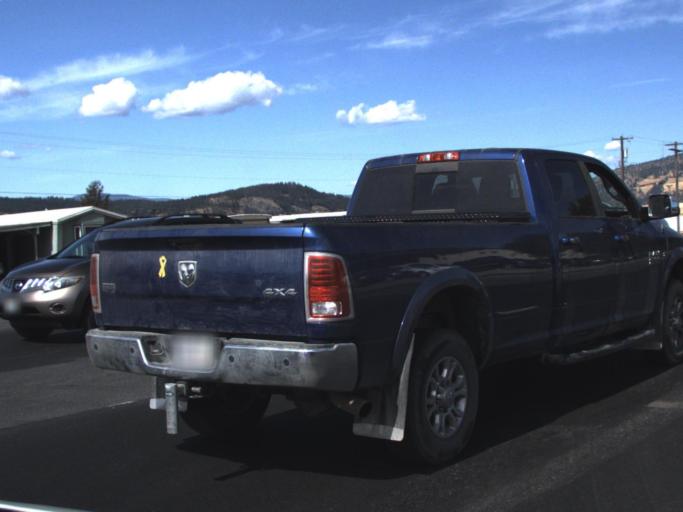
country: US
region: Washington
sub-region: Stevens County
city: Colville
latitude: 48.5347
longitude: -117.9052
